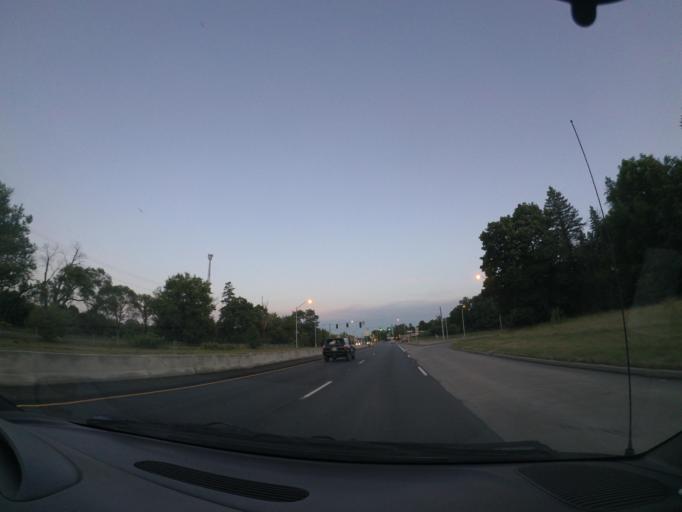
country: US
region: Indiana
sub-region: Elkhart County
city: Dunlap
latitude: 41.6513
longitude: -85.9406
